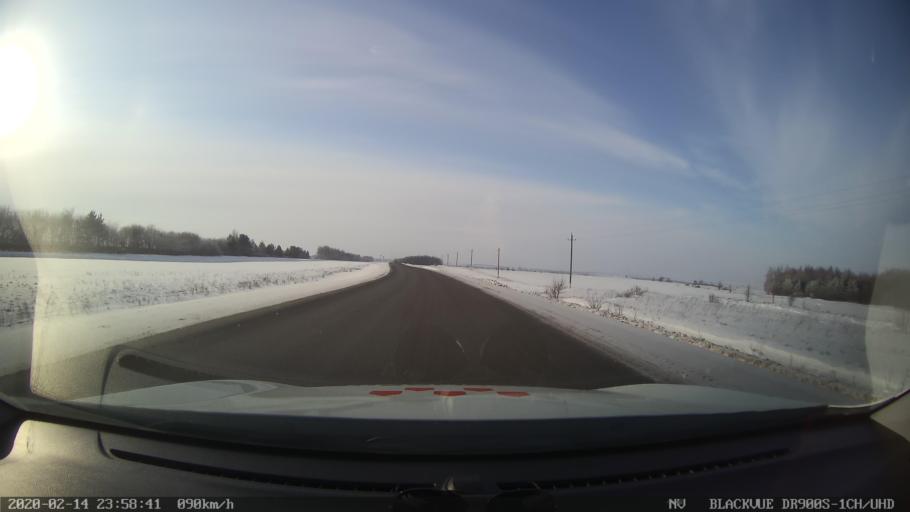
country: RU
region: Tatarstan
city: Kuybyshevskiy Zaton
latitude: 55.3419
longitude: 49.0830
